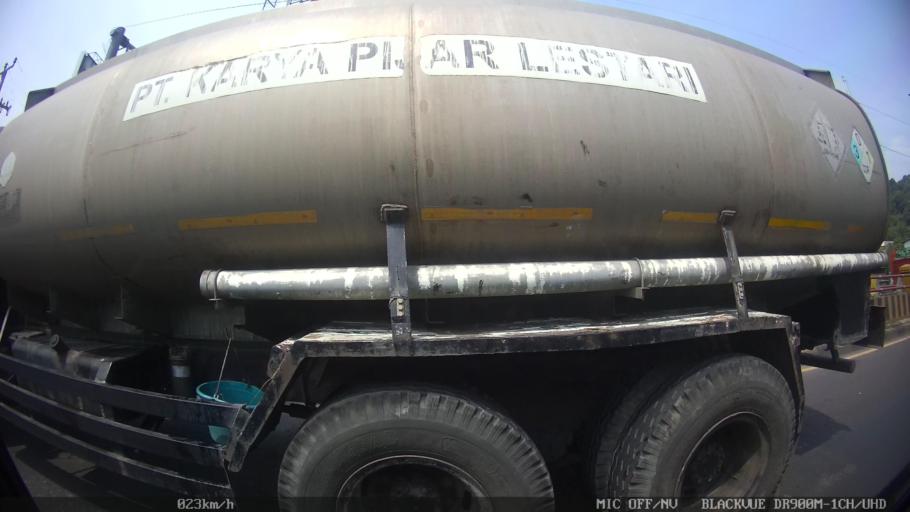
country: ID
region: Banten
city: Kubangkepuh
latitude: -5.9357
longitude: 106.0022
